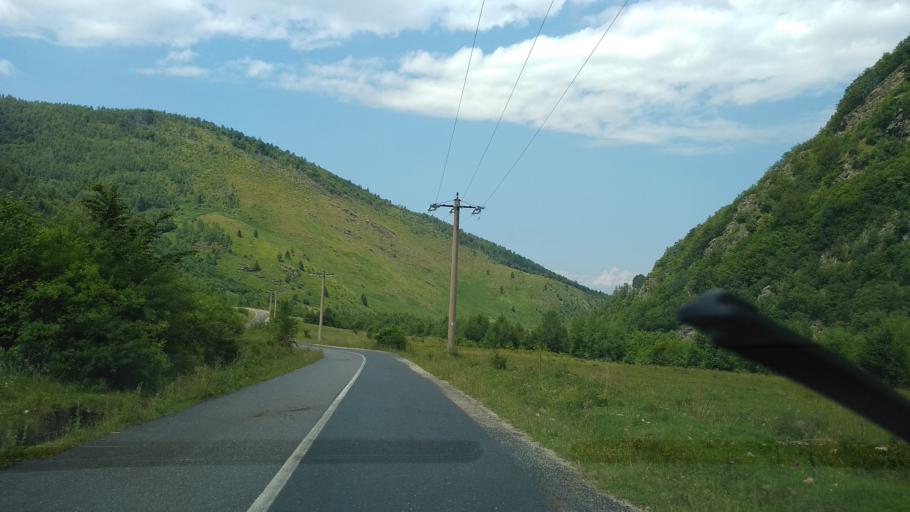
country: RO
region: Hunedoara
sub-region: Comuna Rau de Mori
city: Rau de Mori
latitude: 45.4612
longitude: 22.8982
